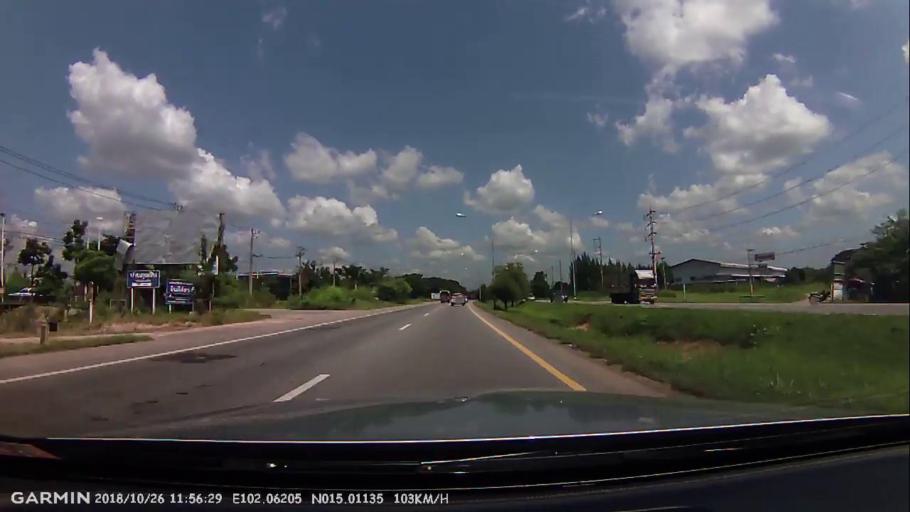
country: TH
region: Nakhon Ratchasima
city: Nakhon Ratchasima
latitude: 15.0115
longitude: 102.0618
